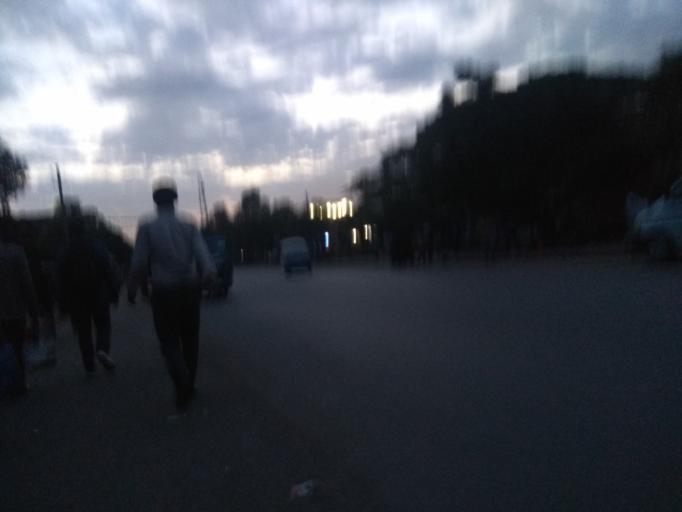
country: ET
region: Oromiya
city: Hagere Hiywet
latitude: 8.9820
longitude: 37.8544
